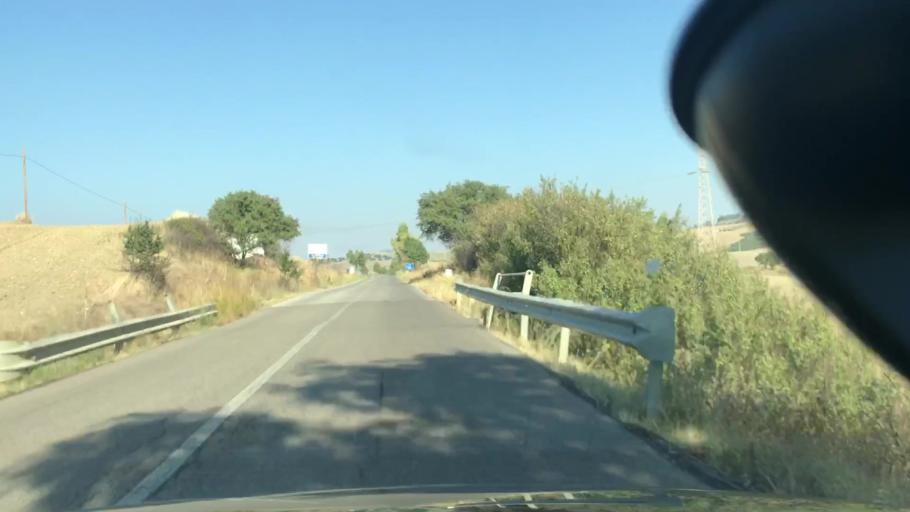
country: IT
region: Basilicate
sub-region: Provincia di Matera
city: La Martella
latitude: 40.6665
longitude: 16.4899
